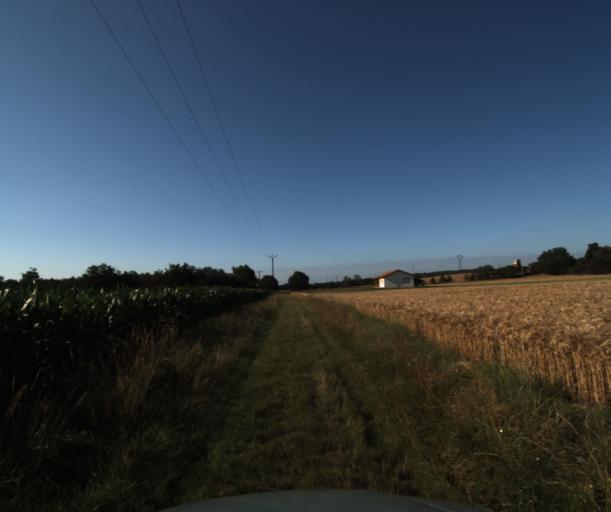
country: FR
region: Midi-Pyrenees
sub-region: Departement de la Haute-Garonne
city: Labarthe-sur-Leze
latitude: 43.4411
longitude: 1.3767
